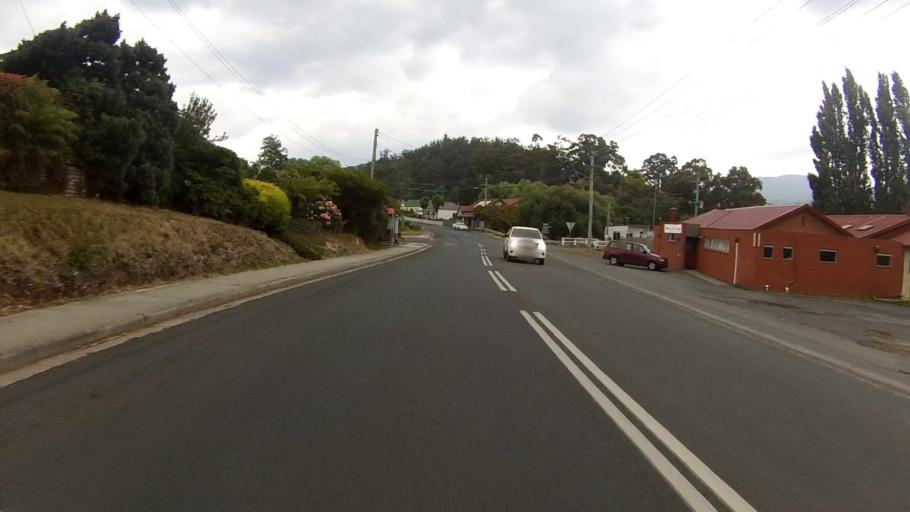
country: AU
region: Tasmania
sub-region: Huon Valley
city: Cygnet
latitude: -43.1559
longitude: 147.0740
